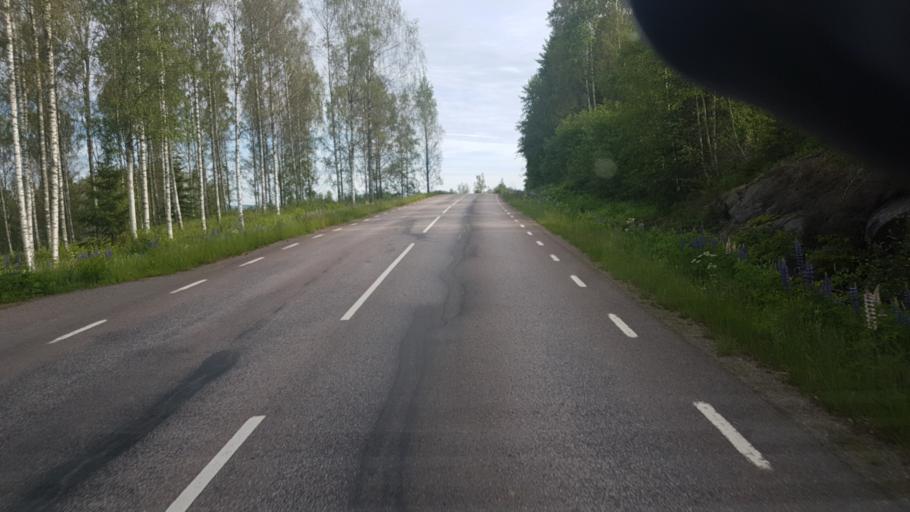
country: SE
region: Vaermland
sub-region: Arvika Kommun
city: Arvika
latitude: 59.7666
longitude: 12.6131
